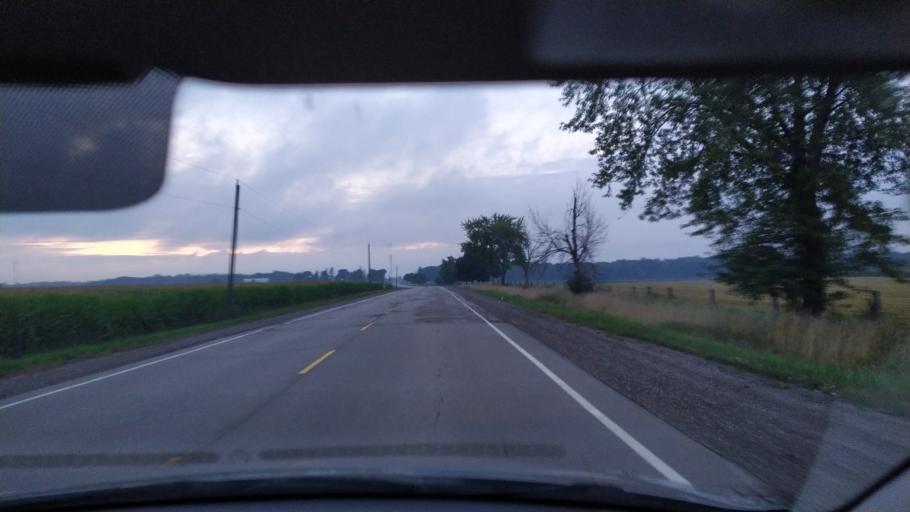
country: CA
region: Ontario
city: Kitchener
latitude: 43.3529
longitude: -80.6980
